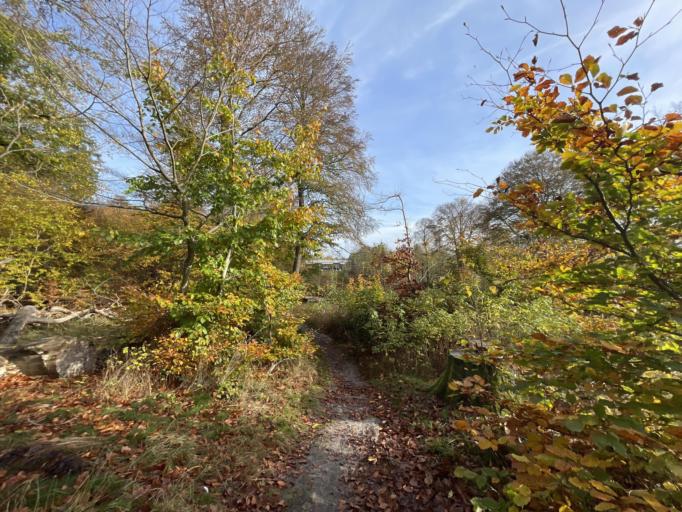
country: DK
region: Capital Region
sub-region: Herlev Kommune
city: Herlev
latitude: 55.7640
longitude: 12.4289
